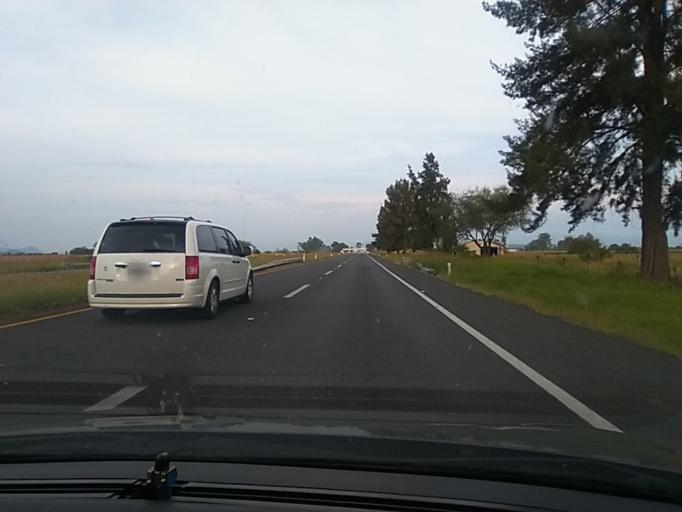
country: MX
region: Michoacan
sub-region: Alvaro Obregon
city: Lazaro Cardenas (La Purisima)
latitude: 19.8913
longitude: -101.0300
